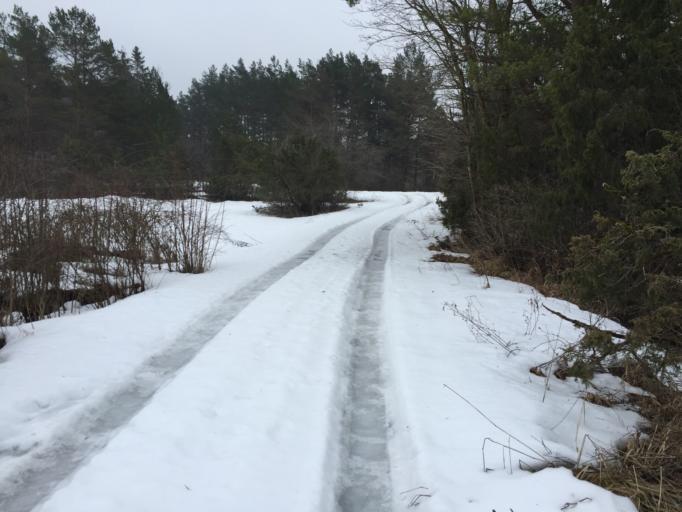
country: EE
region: Saare
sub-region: Orissaare vald
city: Orissaare
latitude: 58.4167
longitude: 22.8234
